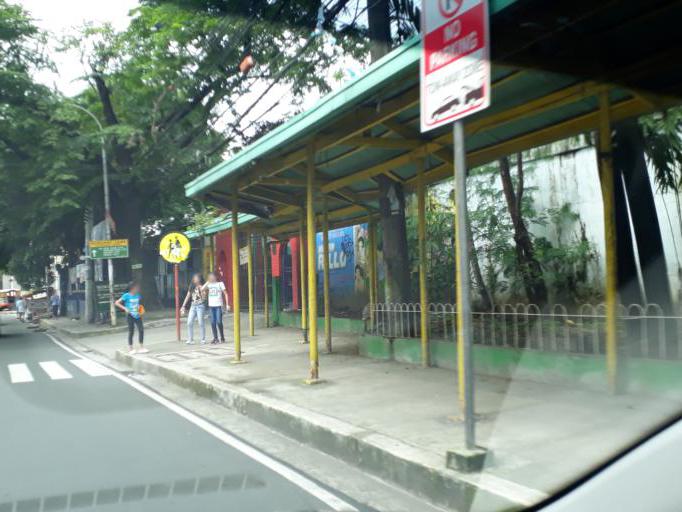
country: PH
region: Metro Manila
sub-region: Quezon City
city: Quezon City
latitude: 14.6299
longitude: 121.0387
